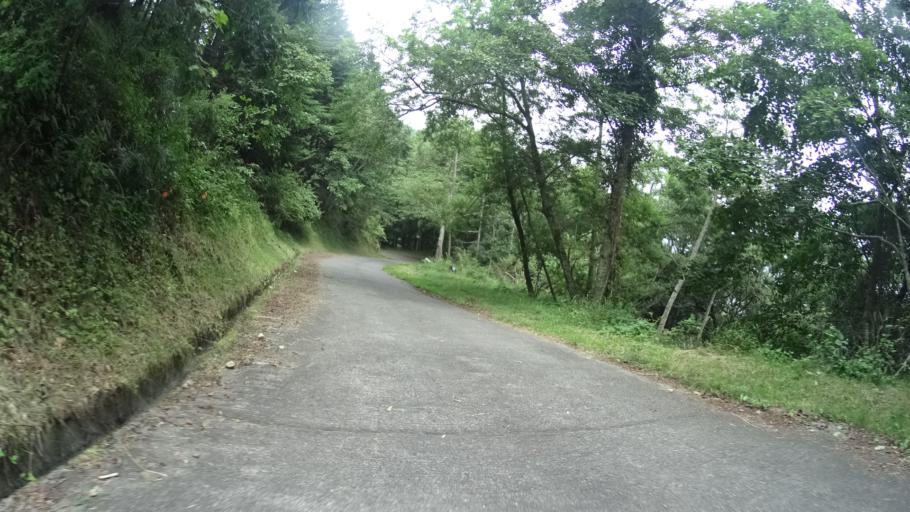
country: JP
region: Yamanashi
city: Kofu-shi
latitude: 35.8273
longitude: 138.5808
